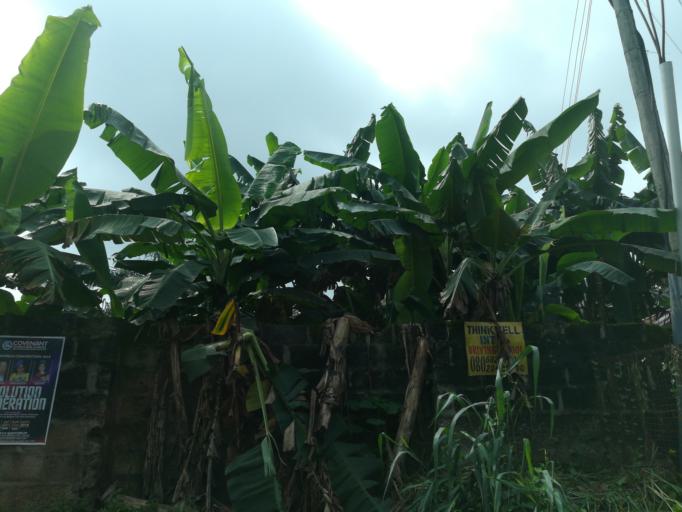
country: NG
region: Rivers
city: Port Harcourt
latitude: 4.8895
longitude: 7.0006
